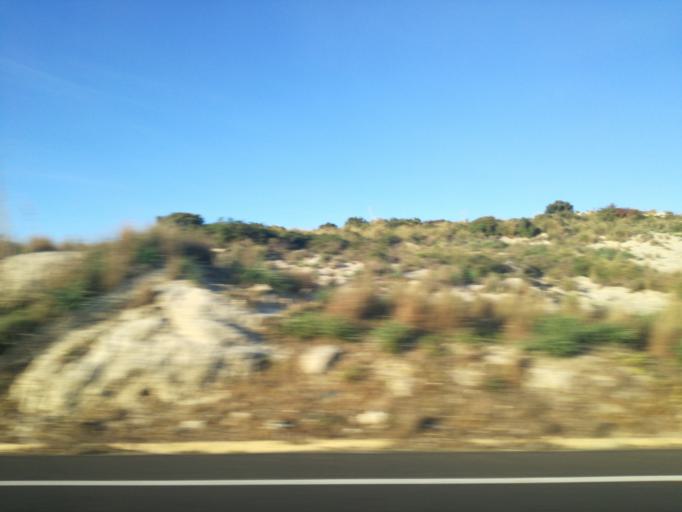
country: IT
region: Sicily
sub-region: Catania
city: San Michele di Ganzaria
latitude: 37.2156
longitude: 14.4196
